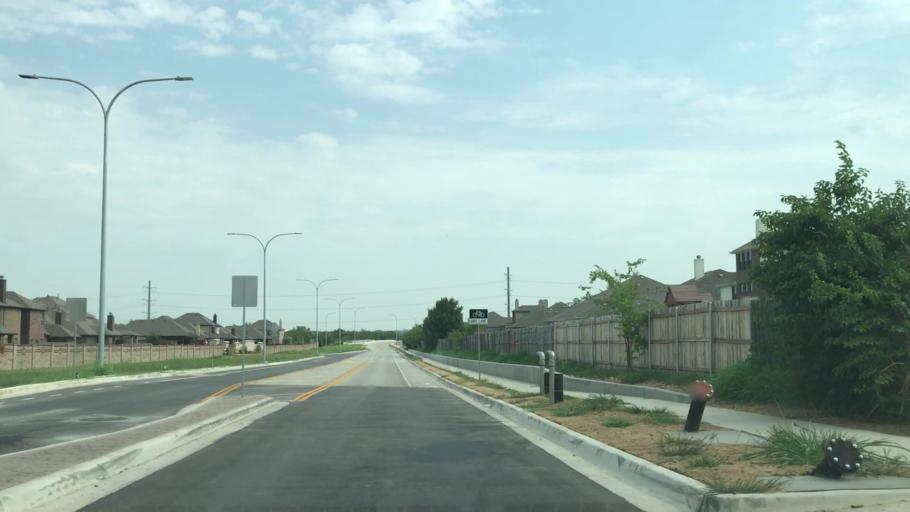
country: US
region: Texas
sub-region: Tarrant County
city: Keller
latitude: 32.9243
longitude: -97.2725
